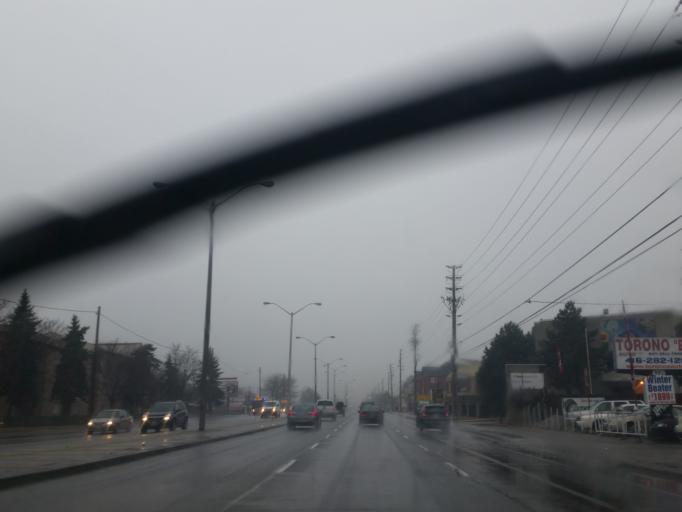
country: CA
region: Ontario
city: Scarborough
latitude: 43.7609
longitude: -79.1959
